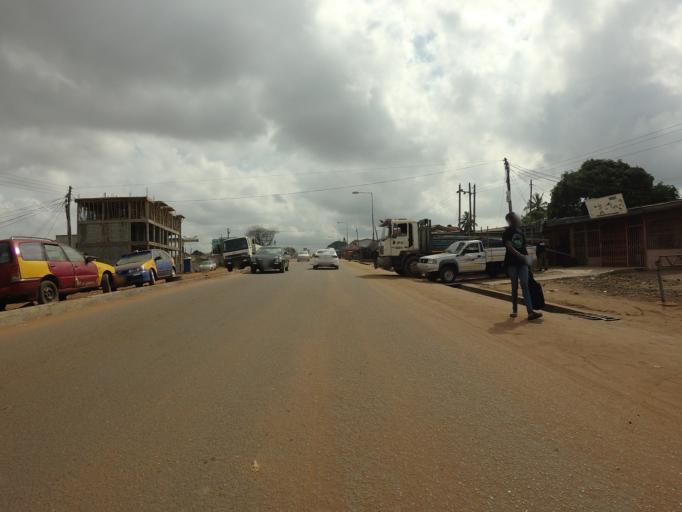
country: GH
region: Greater Accra
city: Teshi Old Town
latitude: 5.6067
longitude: -0.1143
